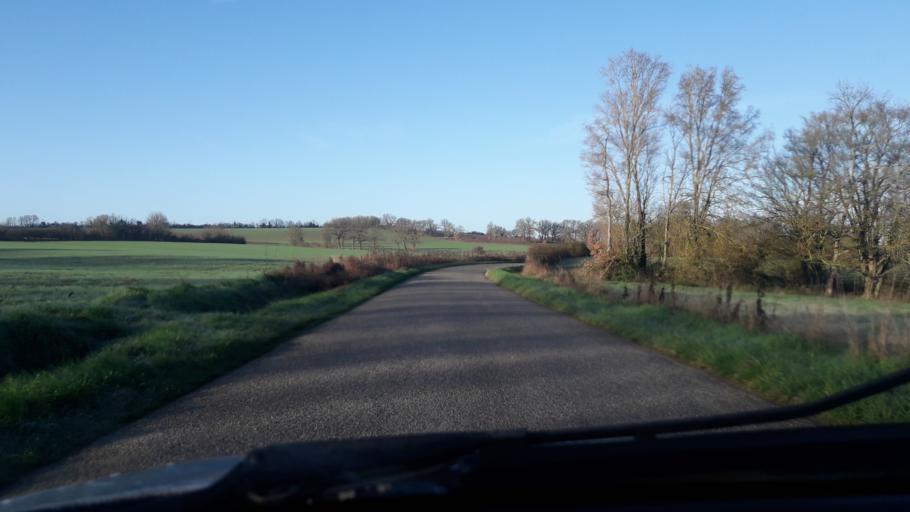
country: FR
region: Midi-Pyrenees
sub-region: Departement du Gers
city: Gimont
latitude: 43.6407
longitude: 0.9911
